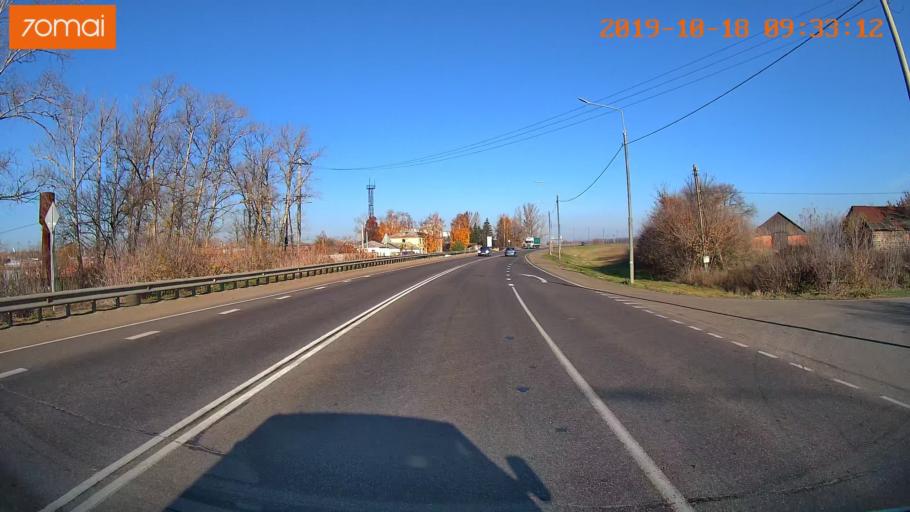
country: RU
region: Tula
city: Yefremov
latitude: 53.1641
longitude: 38.1521
